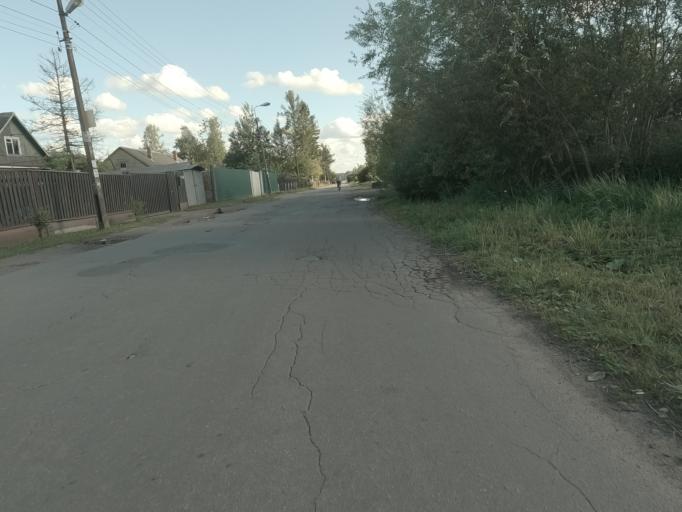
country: RU
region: Leningrad
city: Imeni Morozova
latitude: 59.9628
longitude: 31.0299
